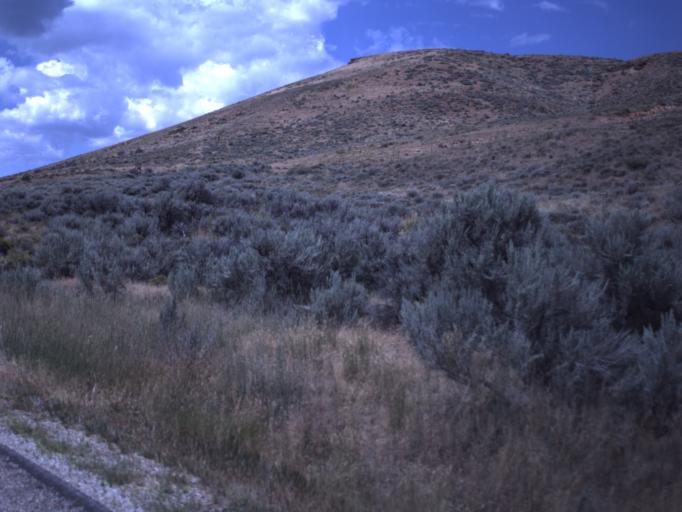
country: US
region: Utah
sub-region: Rich County
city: Randolph
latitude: 41.7686
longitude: -111.1649
